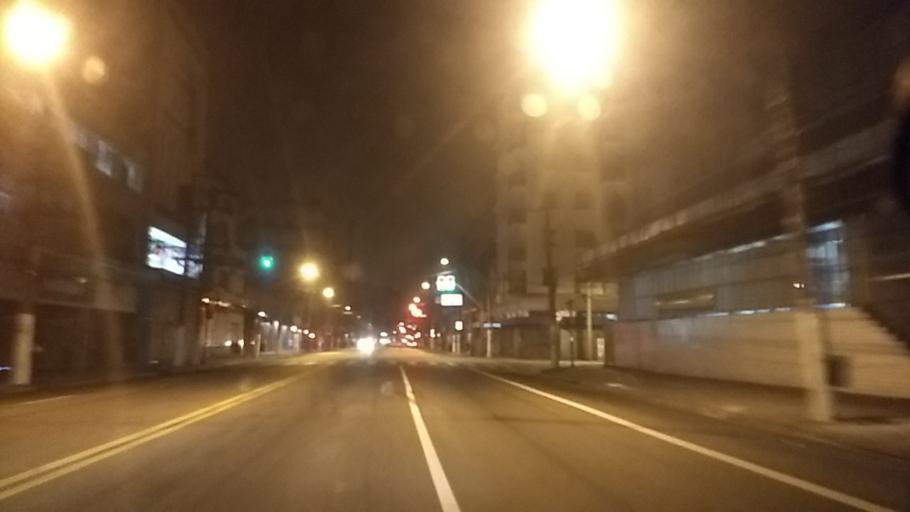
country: BR
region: Sao Paulo
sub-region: Sao Paulo
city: Sao Paulo
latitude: -23.5420
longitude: -46.6151
